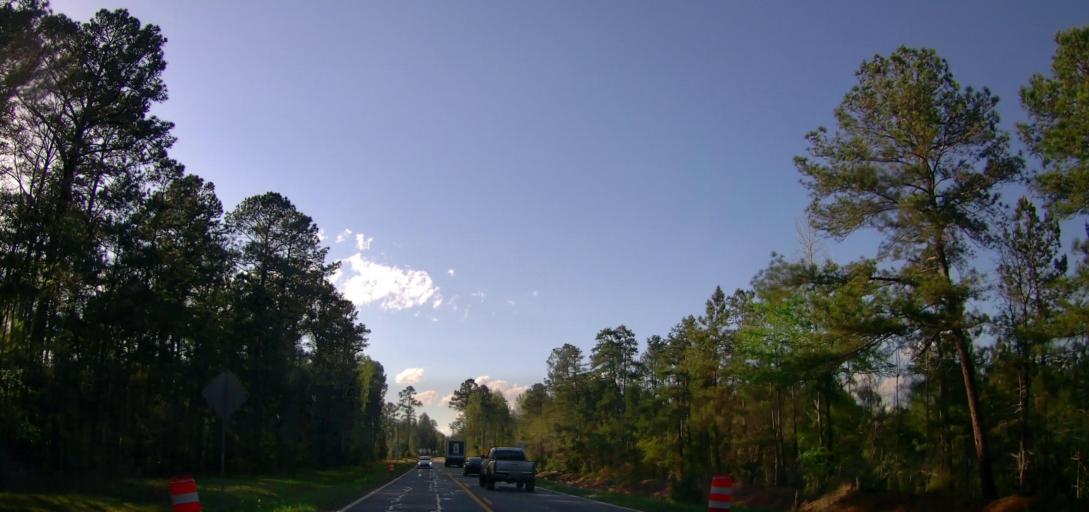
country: US
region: Georgia
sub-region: Baldwin County
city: Milledgeville
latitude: 33.1235
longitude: -83.2950
